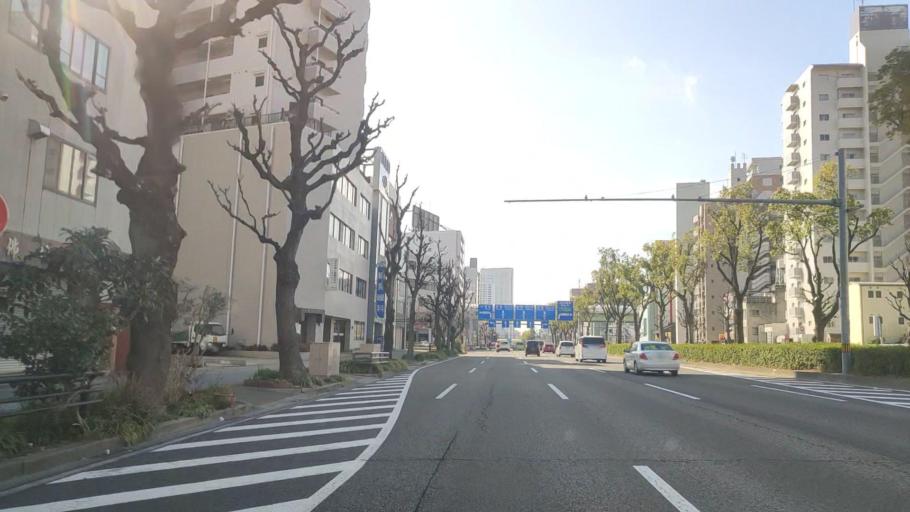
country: JP
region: Aichi
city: Nagoya-shi
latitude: 35.1535
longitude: 136.8989
